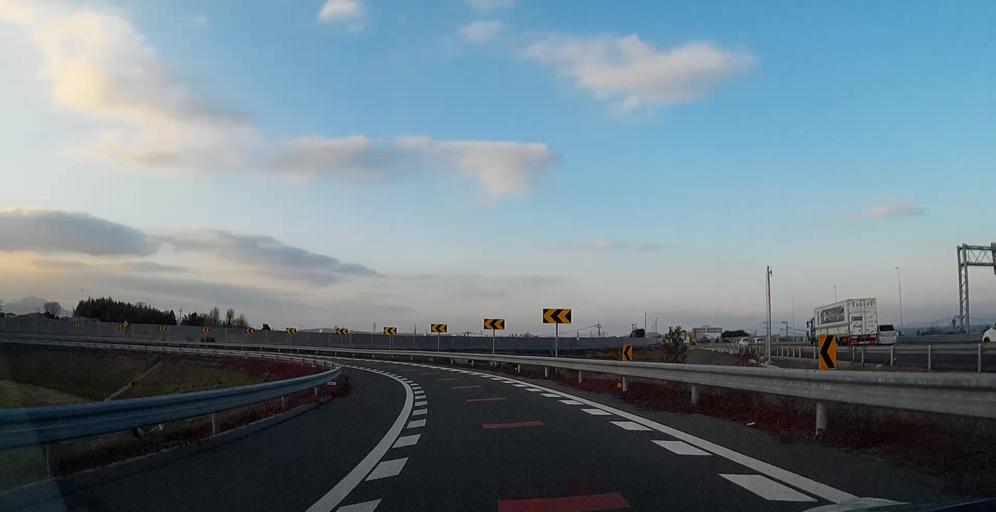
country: JP
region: Kumamoto
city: Kumamoto
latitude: 32.7550
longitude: 130.7885
